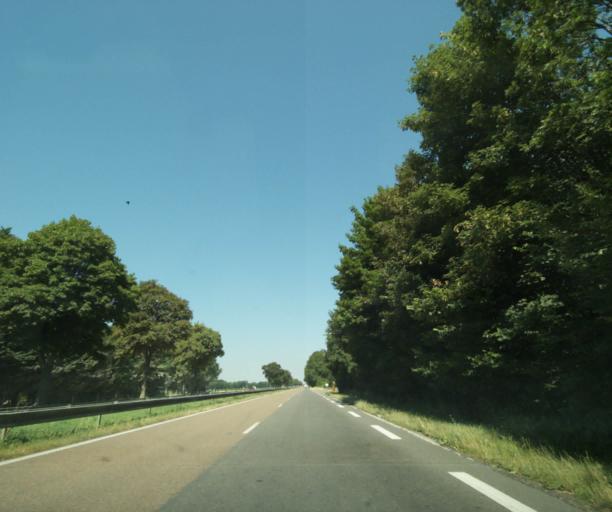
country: FR
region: Champagne-Ardenne
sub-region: Departement de la Marne
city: Pargny-sur-Saulx
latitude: 48.6725
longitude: 4.7726
